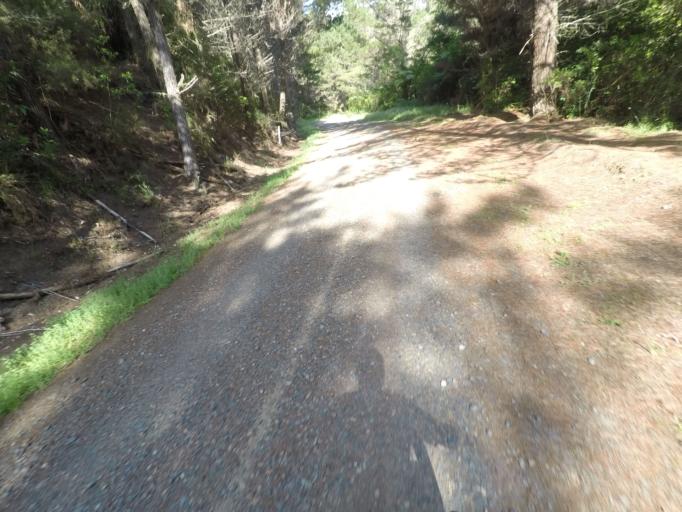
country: NZ
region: Auckland
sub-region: Auckland
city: Muriwai Beach
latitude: -36.7435
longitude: 174.5771
